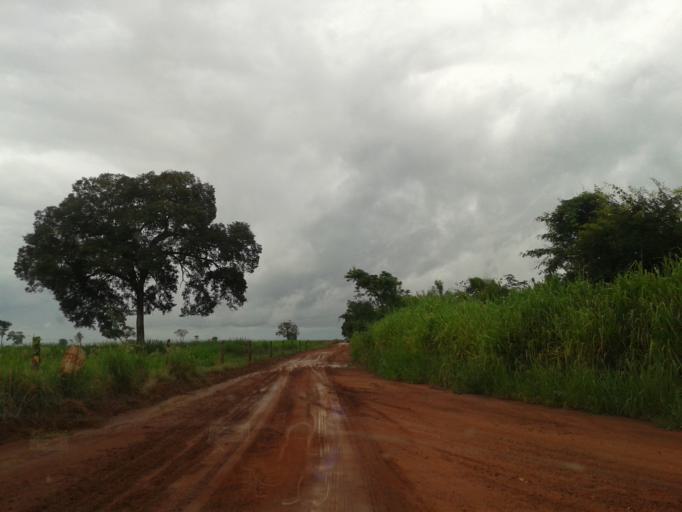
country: BR
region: Minas Gerais
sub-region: Santa Vitoria
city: Santa Vitoria
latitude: -18.7243
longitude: -49.9677
